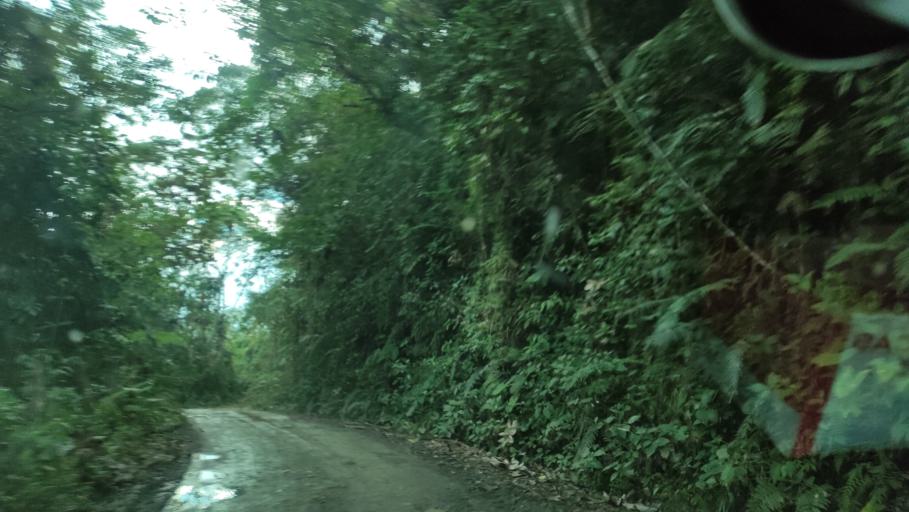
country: CO
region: Valle del Cauca
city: San Pedro
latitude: 3.8795
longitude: -76.1464
